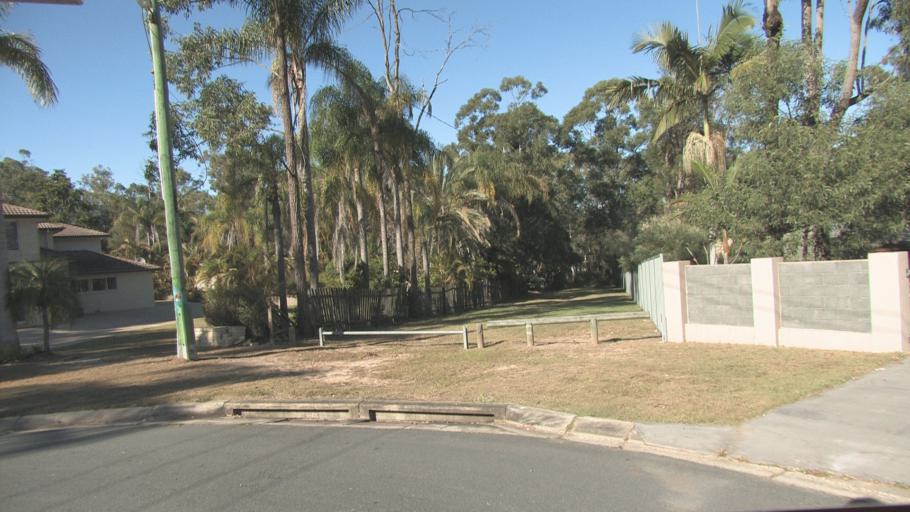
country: AU
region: Queensland
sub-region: Logan
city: Park Ridge South
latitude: -27.6714
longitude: 153.0156
